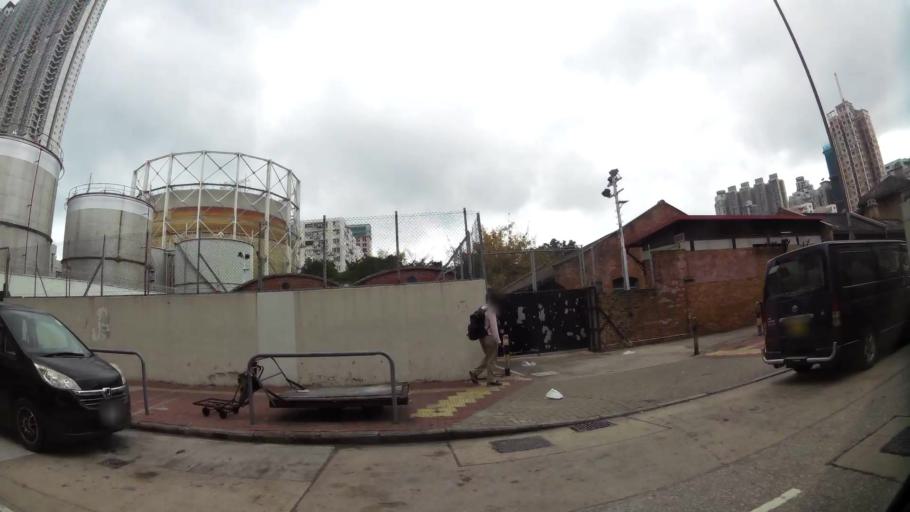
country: HK
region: Kowloon City
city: Kowloon
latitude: 22.3210
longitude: 114.1920
